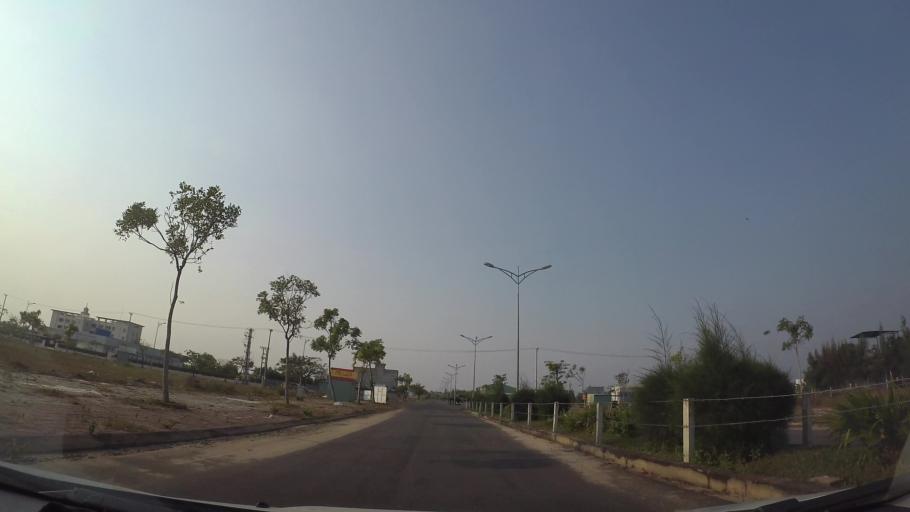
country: VN
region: Da Nang
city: Ngu Hanh Son
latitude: 15.9616
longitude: 108.2611
